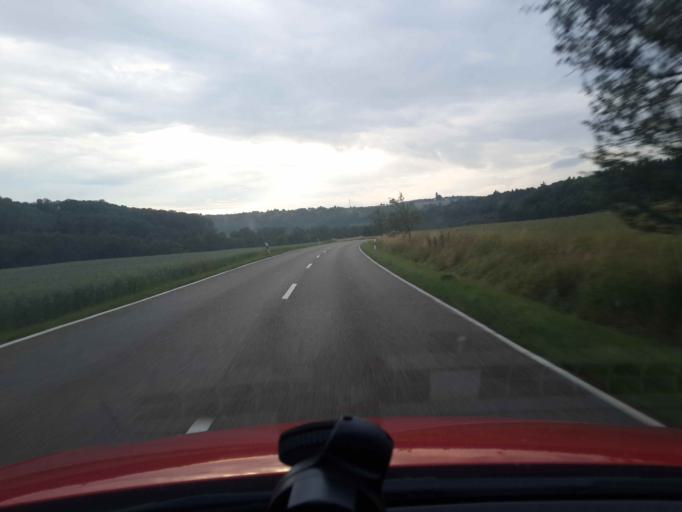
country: DE
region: Baden-Wuerttemberg
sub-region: Regierungsbezirk Stuttgart
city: Neudenau
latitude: 49.2718
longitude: 9.2448
